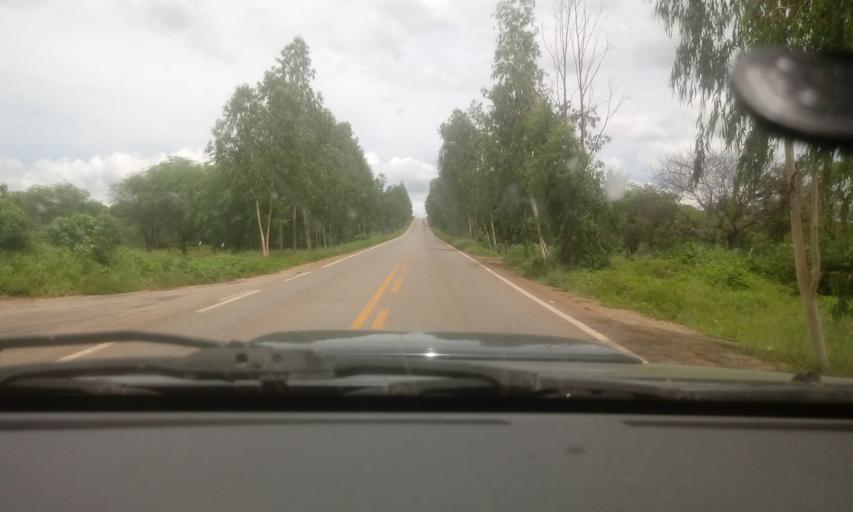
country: BR
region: Bahia
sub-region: Riacho De Santana
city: Riacho de Santana
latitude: -13.5990
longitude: -42.9439
